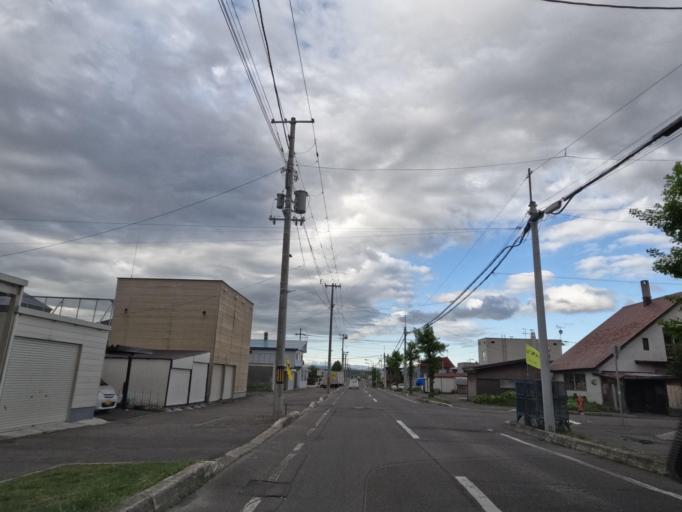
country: JP
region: Hokkaido
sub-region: Asahikawa-shi
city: Asahikawa
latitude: 43.7735
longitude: 142.3130
